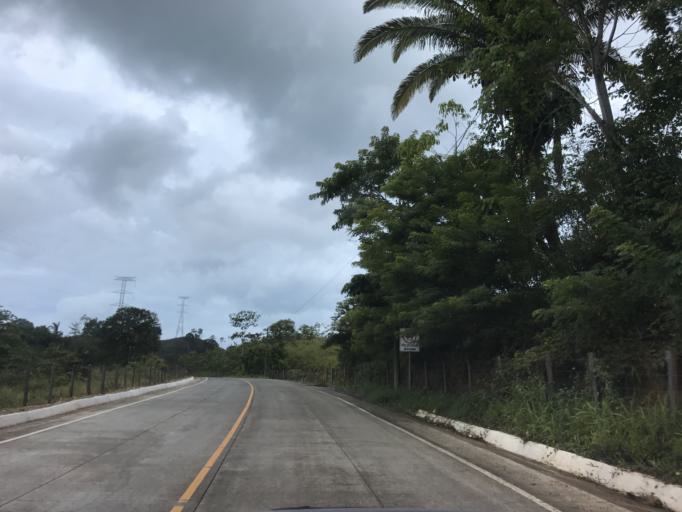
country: GT
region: Izabal
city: Morales
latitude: 15.6359
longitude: -89.0443
